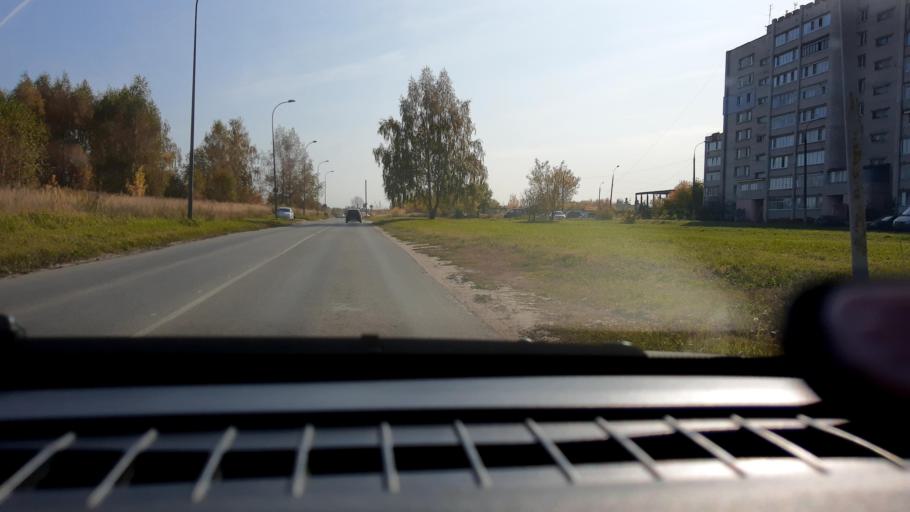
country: RU
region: Nizjnij Novgorod
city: Kstovo
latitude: 56.1519
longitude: 44.2205
